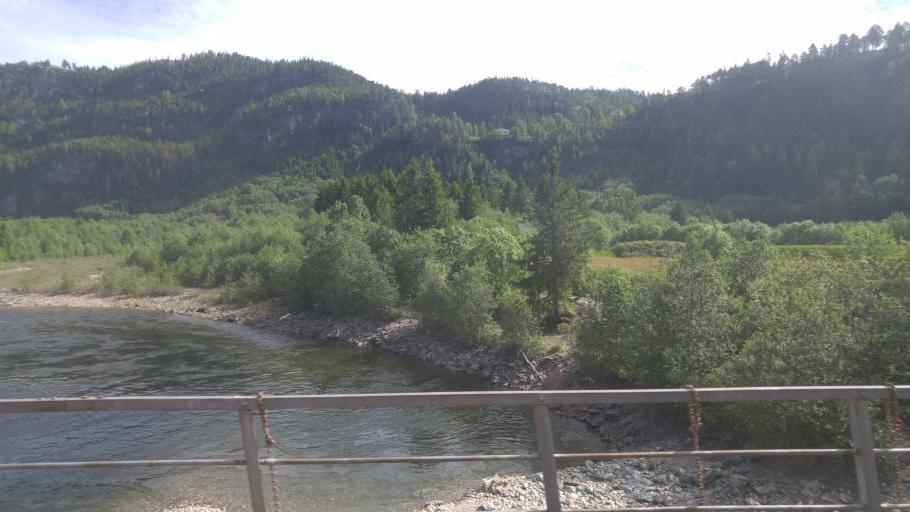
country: NO
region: Sor-Trondelag
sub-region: Midtre Gauldal
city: Storen
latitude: 63.0423
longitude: 10.2922
